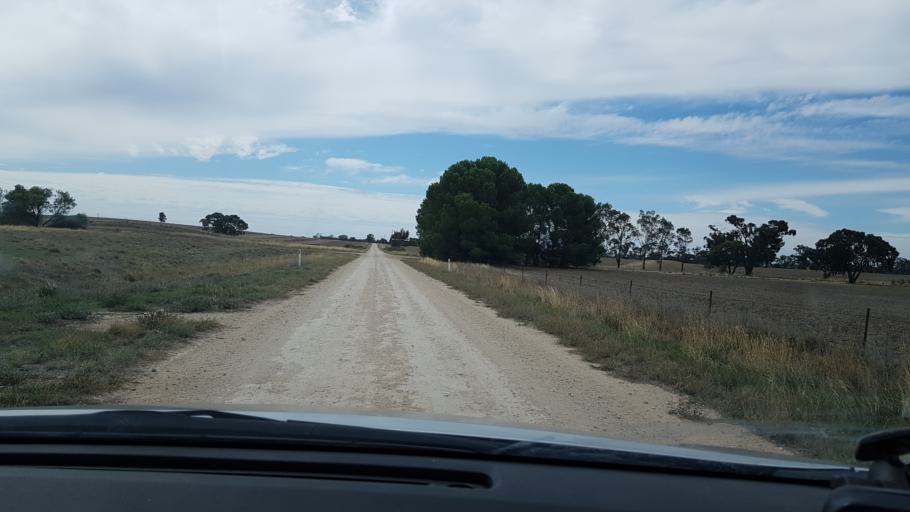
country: AU
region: Victoria
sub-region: Horsham
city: Horsham
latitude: -36.7057
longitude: 141.7806
